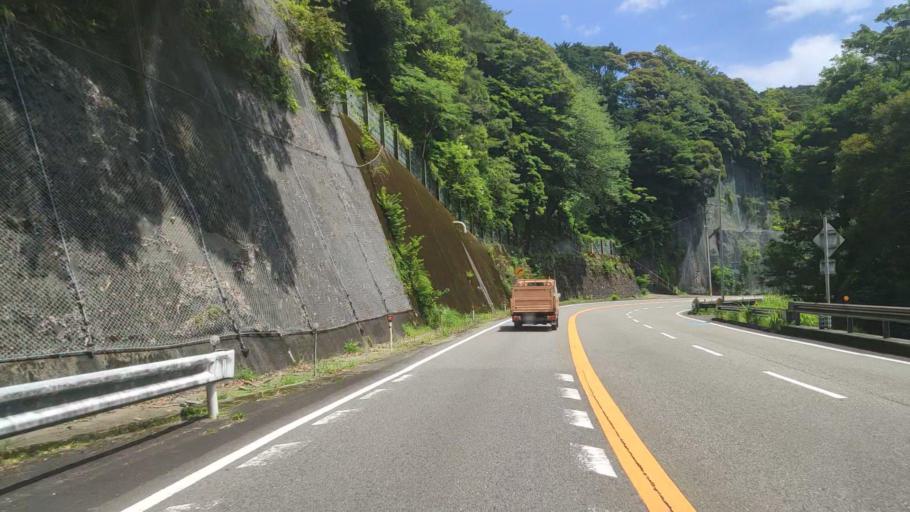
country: JP
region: Mie
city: Owase
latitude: 33.9200
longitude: 136.1026
